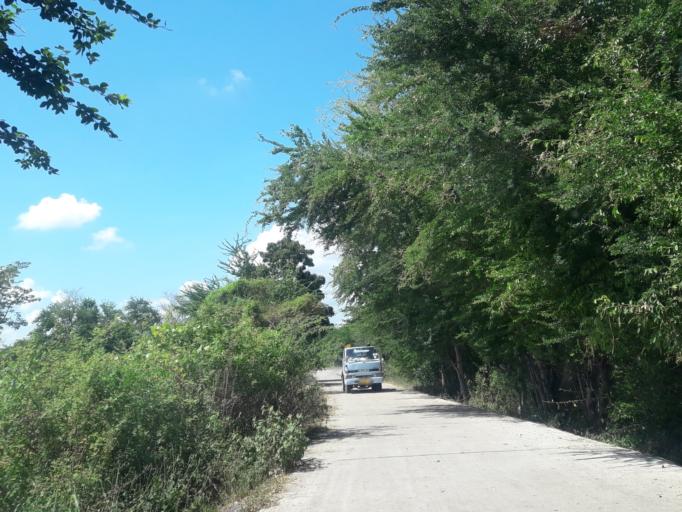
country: TH
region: Lop Buri
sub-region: Amphoe Tha Luang
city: Tha Luang
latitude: 15.0684
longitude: 101.0413
